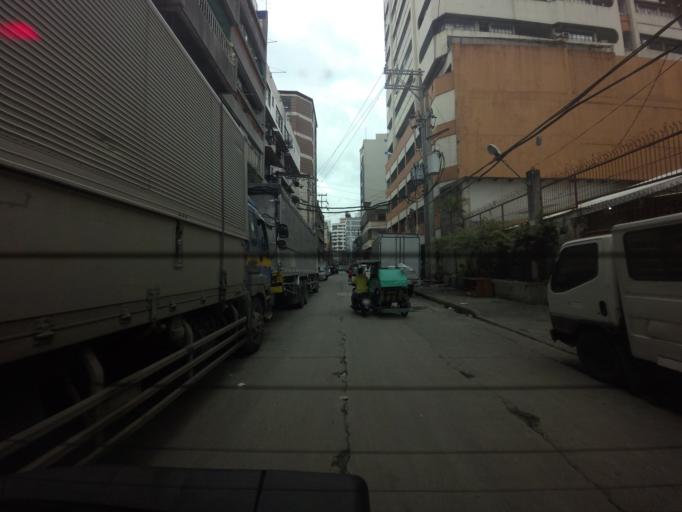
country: PH
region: Metro Manila
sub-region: City of Manila
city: Manila
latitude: 14.5997
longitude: 120.9697
